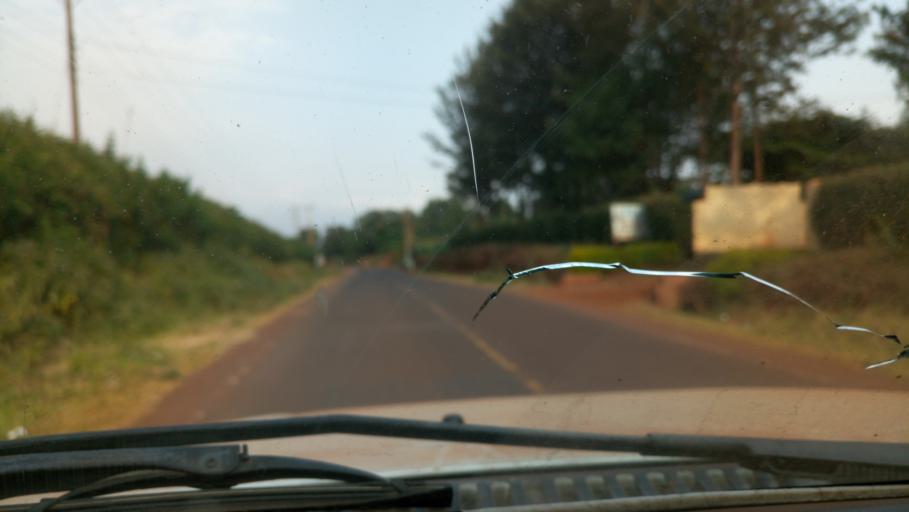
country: KE
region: Murang'a District
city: Maragua
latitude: -0.7910
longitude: 37.0871
